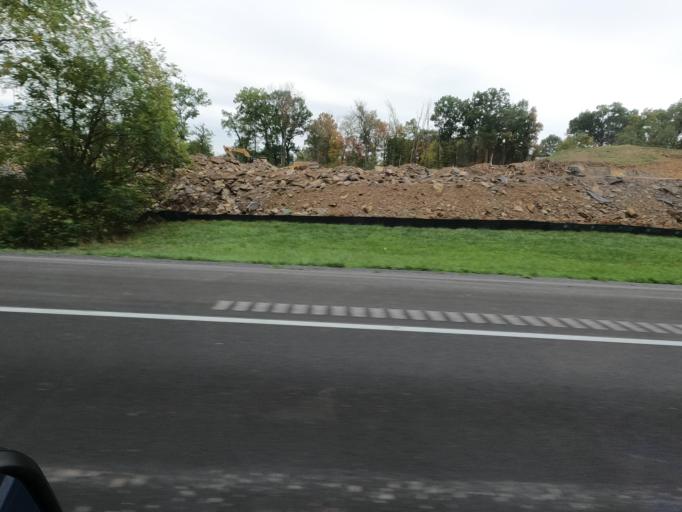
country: US
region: Tennessee
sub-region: Sullivan County
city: Colonial Heights
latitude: 36.5265
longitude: -82.5087
